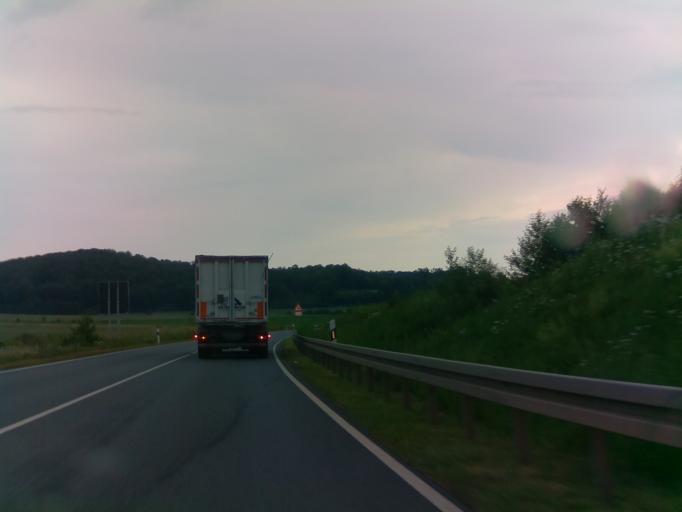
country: DE
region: Lower Saxony
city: Elze
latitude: 52.1162
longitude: 9.6852
